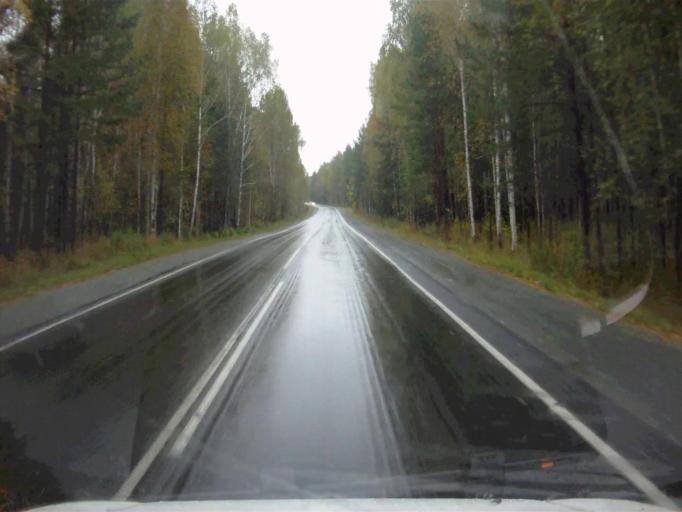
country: RU
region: Chelyabinsk
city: Tayginka
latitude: 55.5916
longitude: 60.6267
